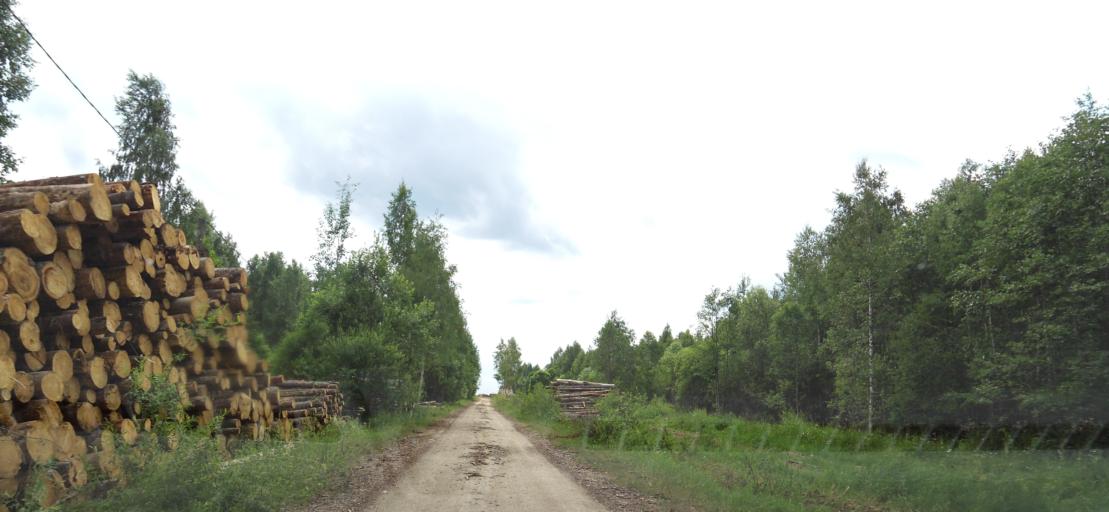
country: LV
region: Ogre
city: Jumprava
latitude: 56.4361
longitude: 24.9025
